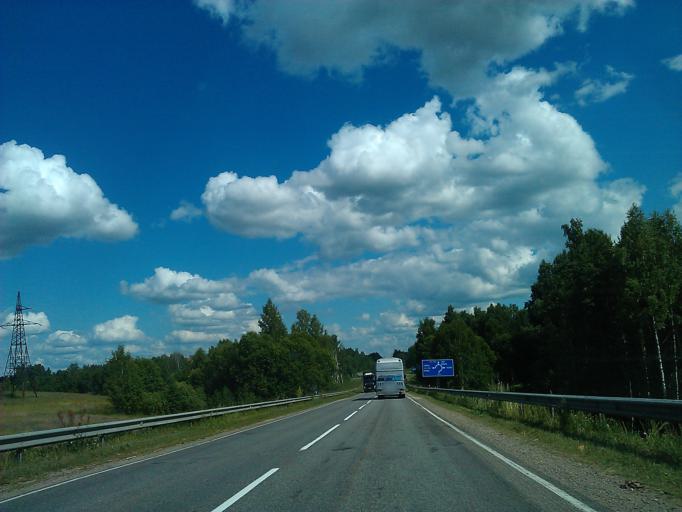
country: LV
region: Rezekne
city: Rezekne
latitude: 56.5460
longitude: 27.3468
